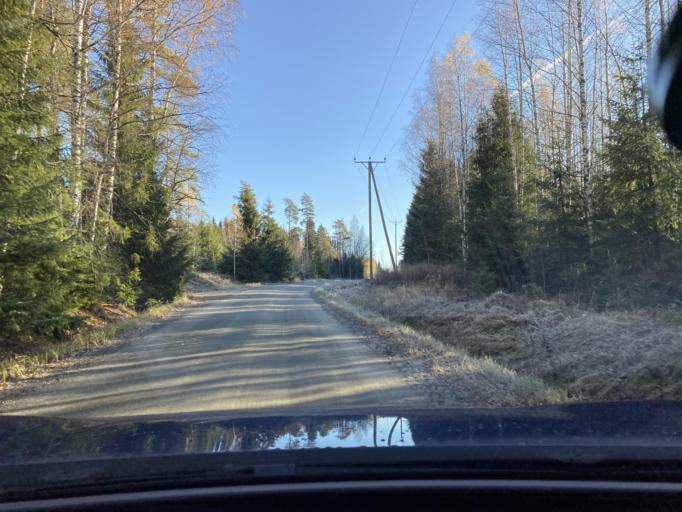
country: FI
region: Pirkanmaa
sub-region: Etelae-Pirkanmaa
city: Toijala
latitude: 61.0258
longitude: 23.8213
